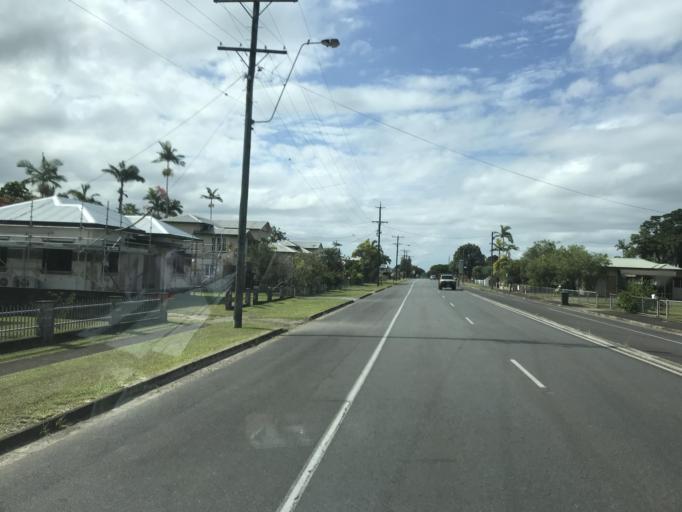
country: AU
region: Queensland
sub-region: Cassowary Coast
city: Innisfail
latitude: -17.5361
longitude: 146.0329
